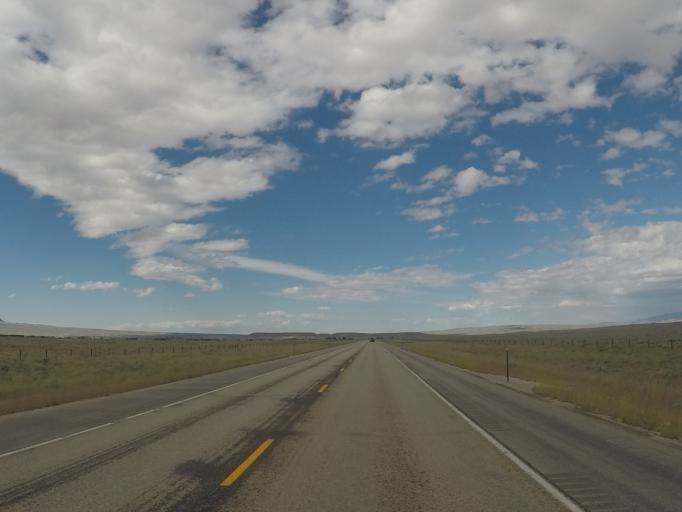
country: US
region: Wyoming
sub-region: Park County
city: Cody
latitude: 44.8568
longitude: -109.1412
